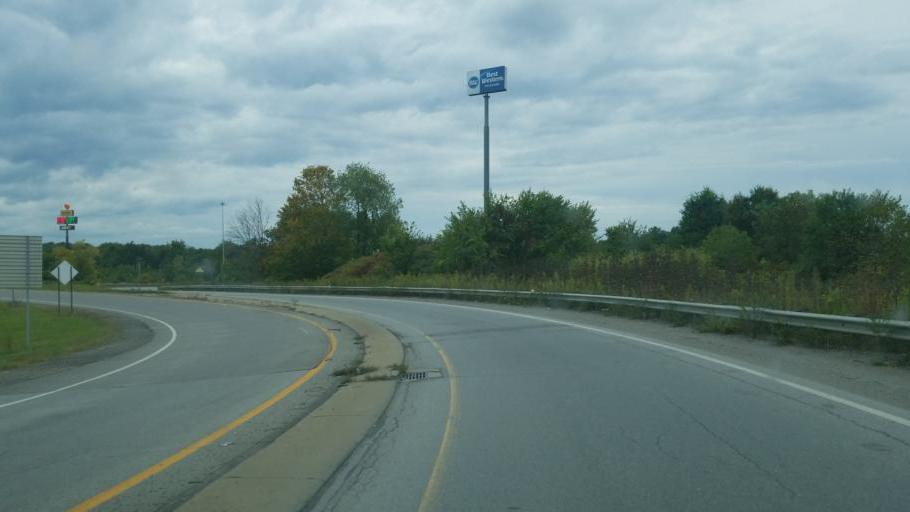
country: US
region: Ohio
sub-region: Trumbull County
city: Hubbard
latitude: 41.1777
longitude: -80.5706
